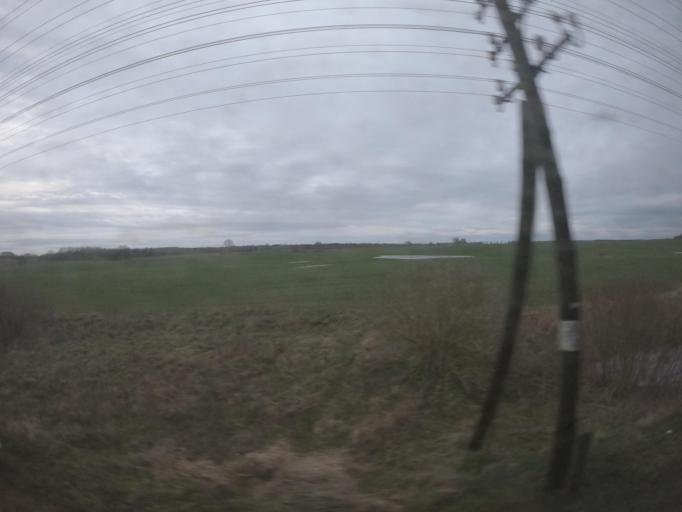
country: PL
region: West Pomeranian Voivodeship
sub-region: Powiat szczecinecki
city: Lubowo
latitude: 53.5691
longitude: 16.3567
